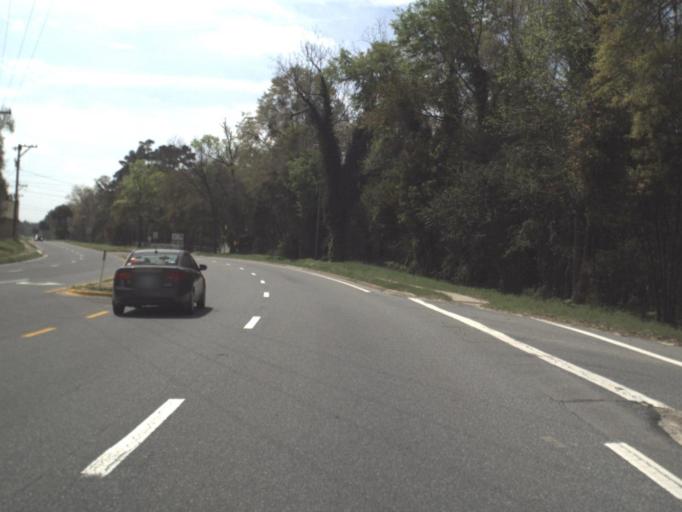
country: US
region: Florida
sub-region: Gadsden County
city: Havana
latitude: 30.6516
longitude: -84.4170
